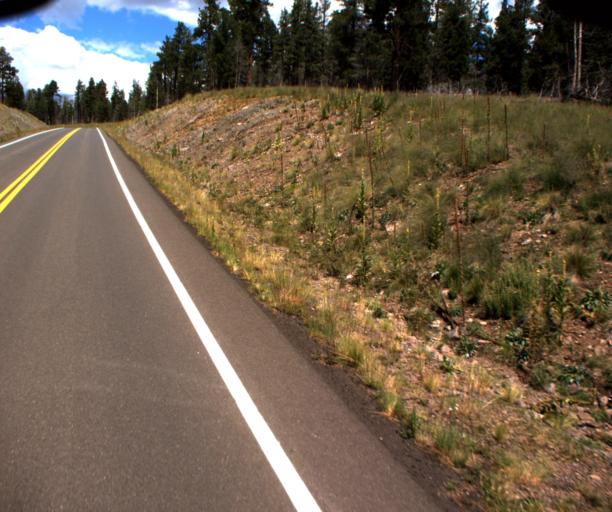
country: US
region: Arizona
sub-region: Apache County
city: Eagar
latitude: 33.9258
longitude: -109.4570
